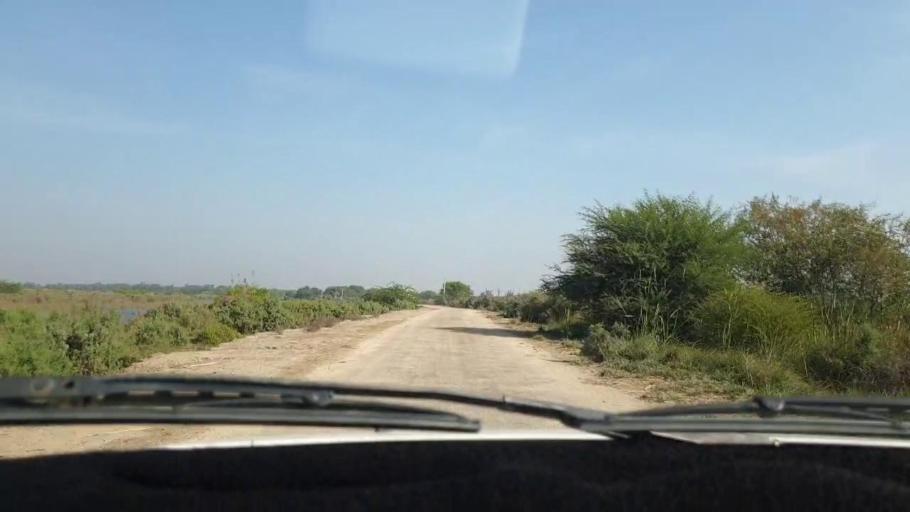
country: PK
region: Sindh
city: Tando Muhammad Khan
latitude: 24.9884
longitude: 68.4629
